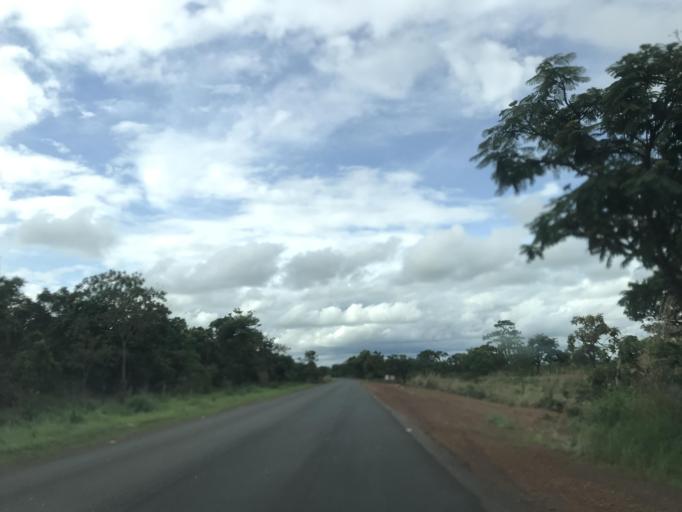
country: BR
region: Goias
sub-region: Bela Vista De Goias
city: Bela Vista de Goias
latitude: -17.0273
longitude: -48.6534
